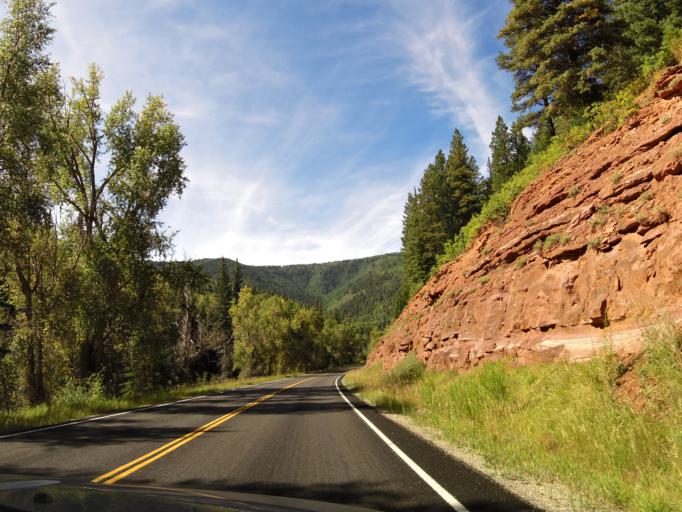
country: US
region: Colorado
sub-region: Montezuma County
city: Mancos
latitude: 37.5785
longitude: -108.1794
